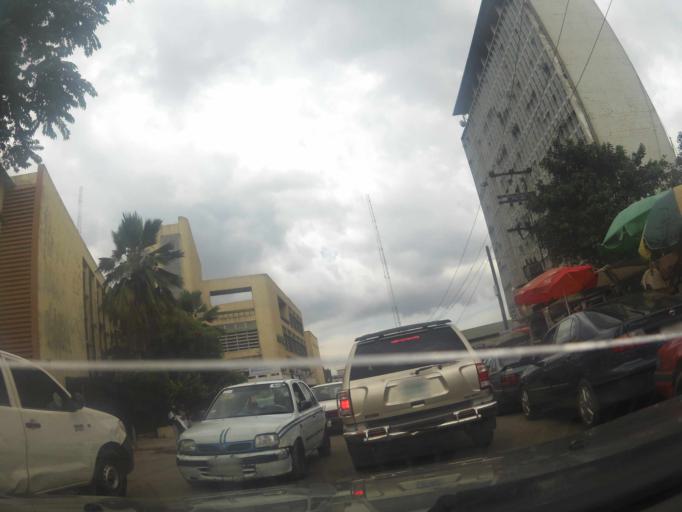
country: NG
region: Oyo
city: Ibadan
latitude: 7.3876
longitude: 3.8811
